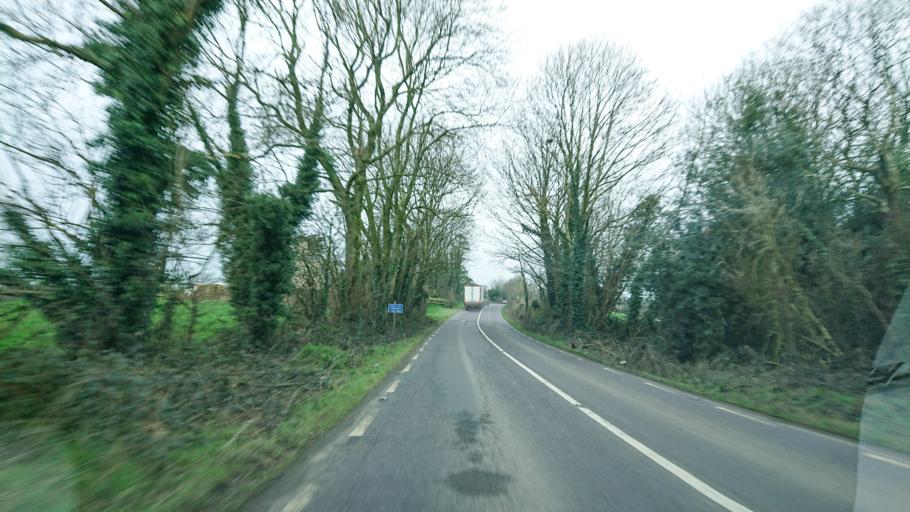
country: IE
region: Munster
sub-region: County Cork
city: Bandon
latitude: 51.7444
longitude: -8.8196
